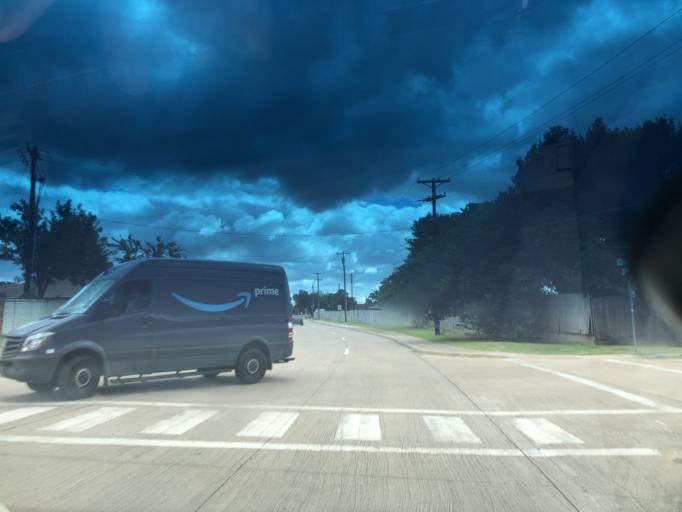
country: US
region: Texas
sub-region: Dallas County
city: Grand Prairie
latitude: 32.6983
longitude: -97.0208
